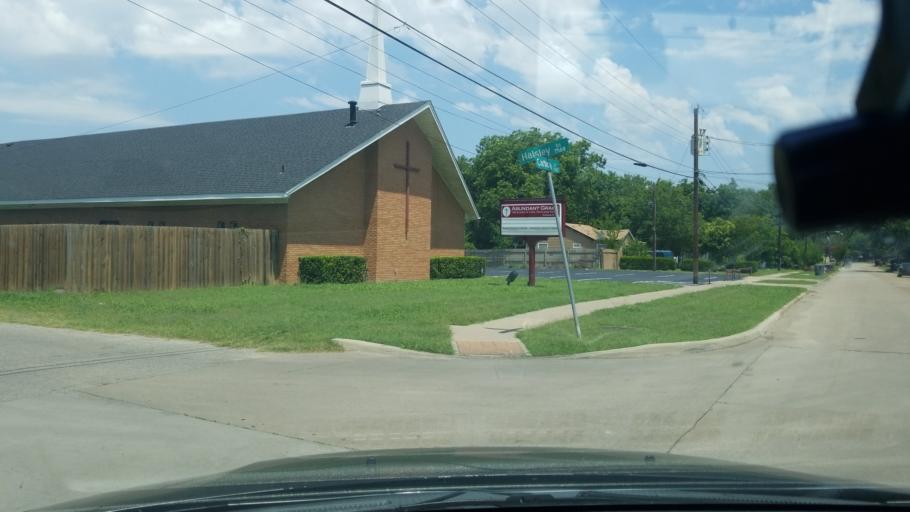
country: US
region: Texas
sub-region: Dallas County
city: Balch Springs
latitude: 32.7314
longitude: -96.6917
